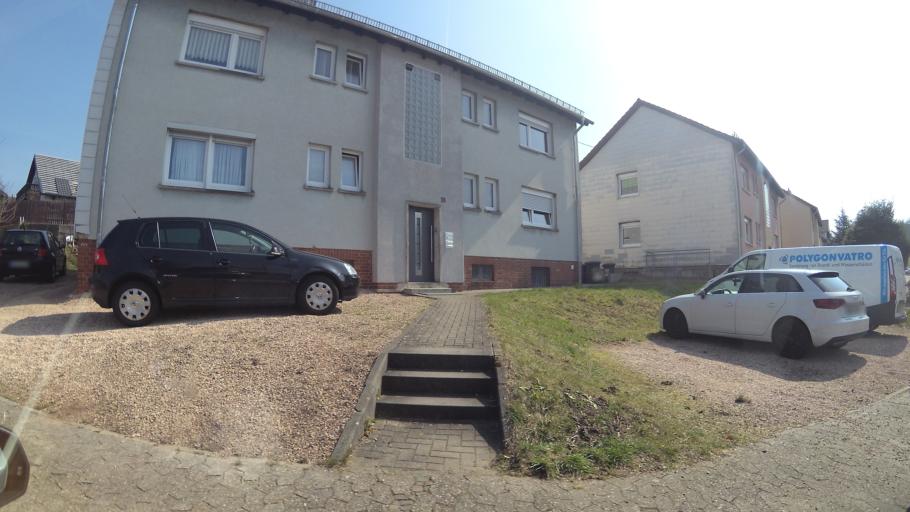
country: DE
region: Saarland
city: Quierschied
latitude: 49.3119
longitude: 7.0484
